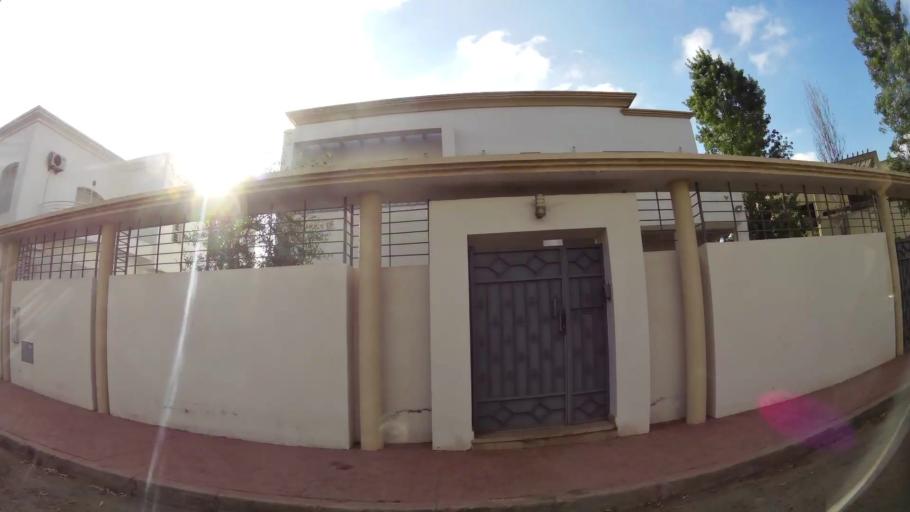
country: MA
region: Rabat-Sale-Zemmour-Zaer
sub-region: Skhirate-Temara
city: Temara
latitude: 33.9575
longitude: -6.8584
